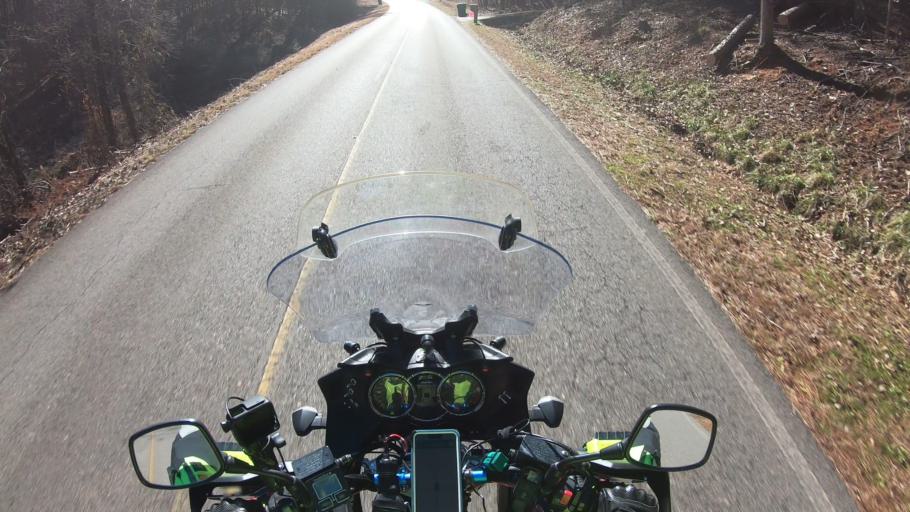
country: US
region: Alabama
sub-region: Clay County
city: Lineville
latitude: 33.3806
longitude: -85.8171
